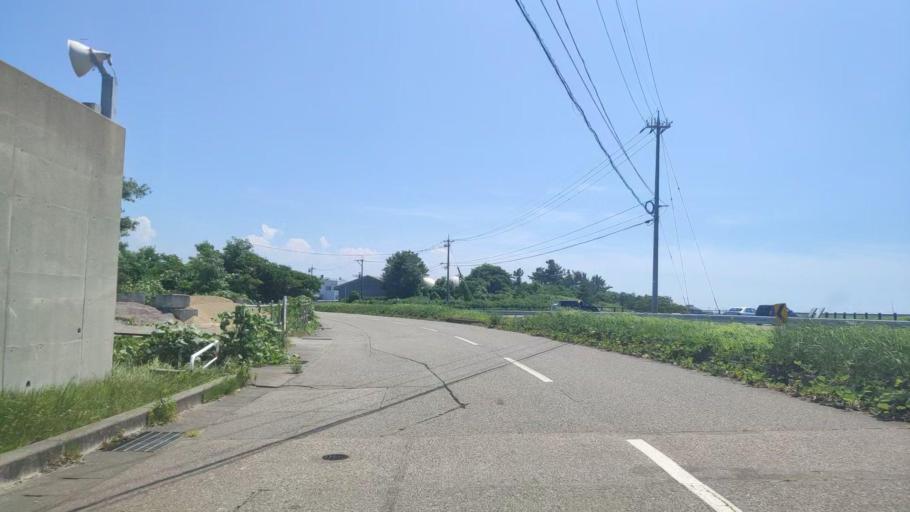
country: JP
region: Ishikawa
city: Kanazawa-shi
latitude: 36.6247
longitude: 136.6096
